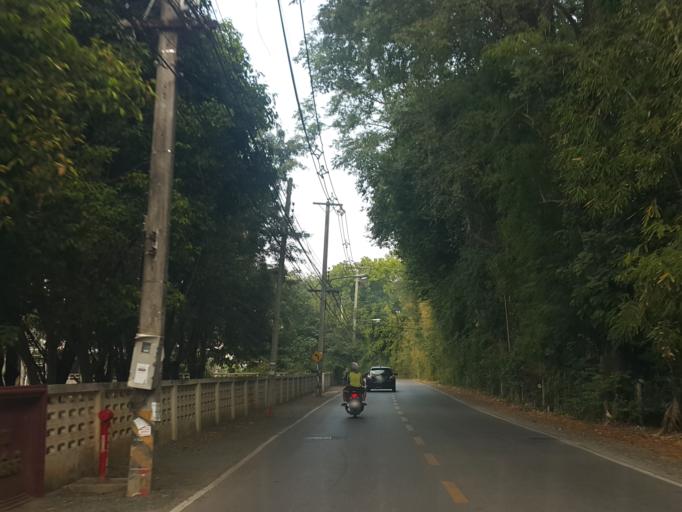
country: TH
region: Chiang Mai
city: Chiang Mai
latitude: 18.8256
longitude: 98.9947
